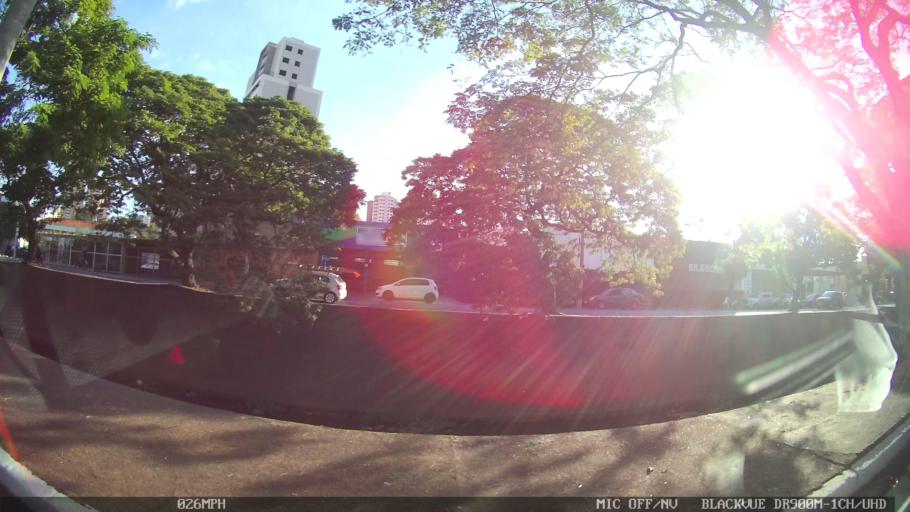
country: BR
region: Sao Paulo
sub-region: Ribeirao Preto
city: Ribeirao Preto
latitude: -21.1844
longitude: -47.7994
